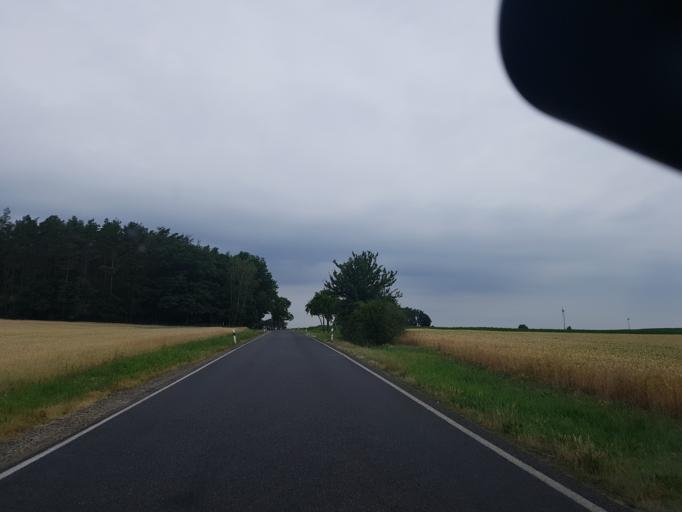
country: DE
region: Brandenburg
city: Hohenbucko
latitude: 51.6978
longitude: 13.5032
